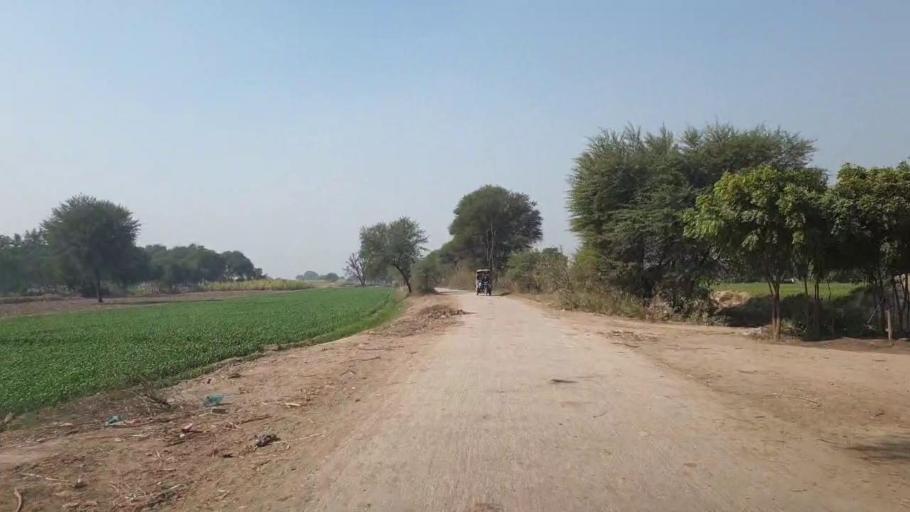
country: PK
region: Sindh
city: Tando Jam
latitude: 25.3297
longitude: 68.6202
